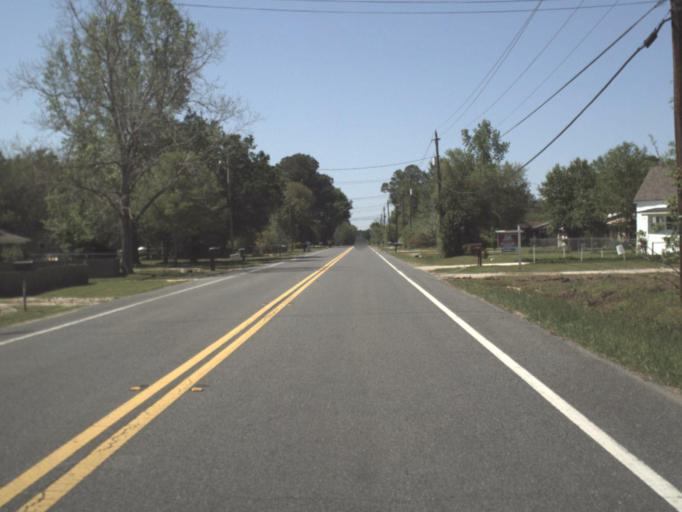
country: US
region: Florida
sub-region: Escambia County
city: Bellview
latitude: 30.5214
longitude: -87.3853
